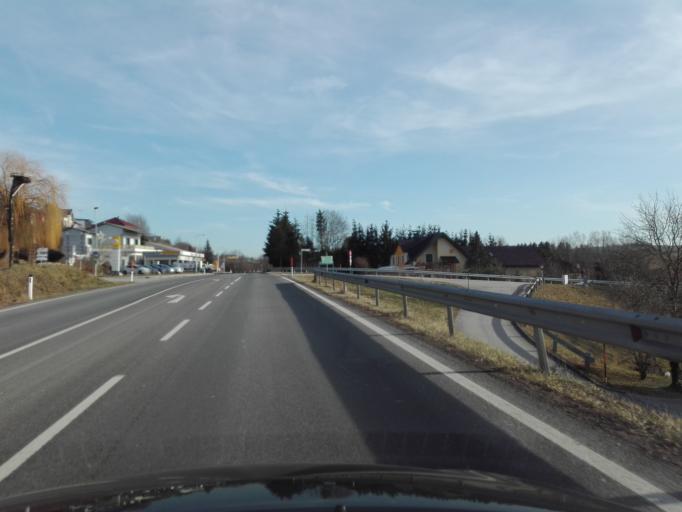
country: AT
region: Lower Austria
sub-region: Politischer Bezirk Amstetten
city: Zeillern
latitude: 48.1754
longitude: 14.8293
